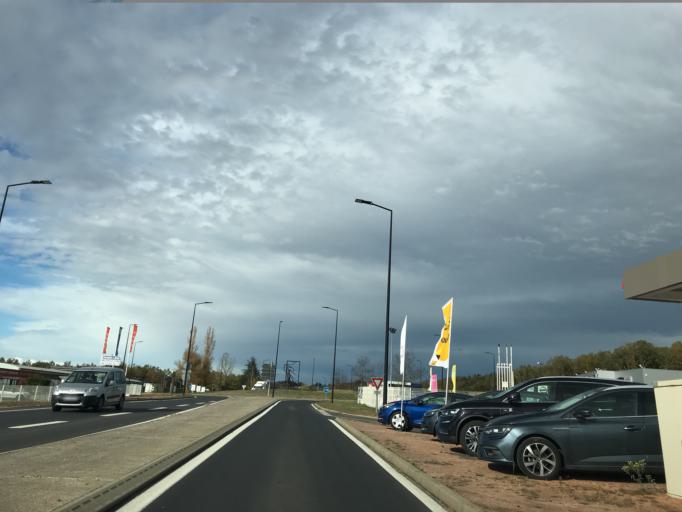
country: FR
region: Auvergne
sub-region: Departement du Puy-de-Dome
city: Peschadoires
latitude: 45.8552
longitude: 3.5085
